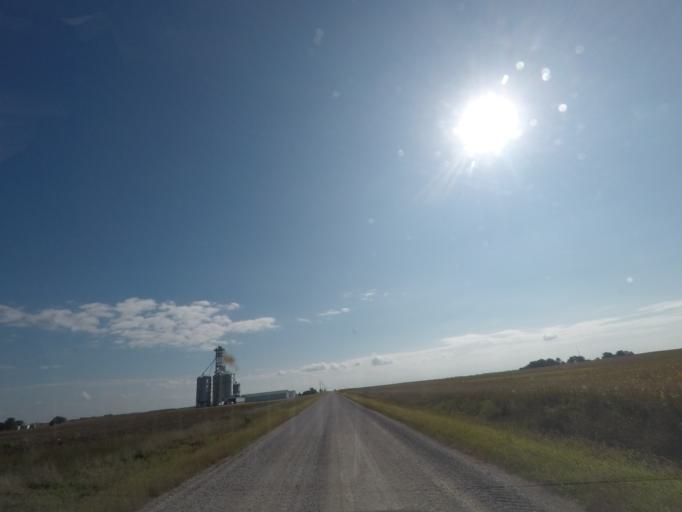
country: US
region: Iowa
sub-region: Story County
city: Nevada
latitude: 42.0489
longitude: -93.4135
